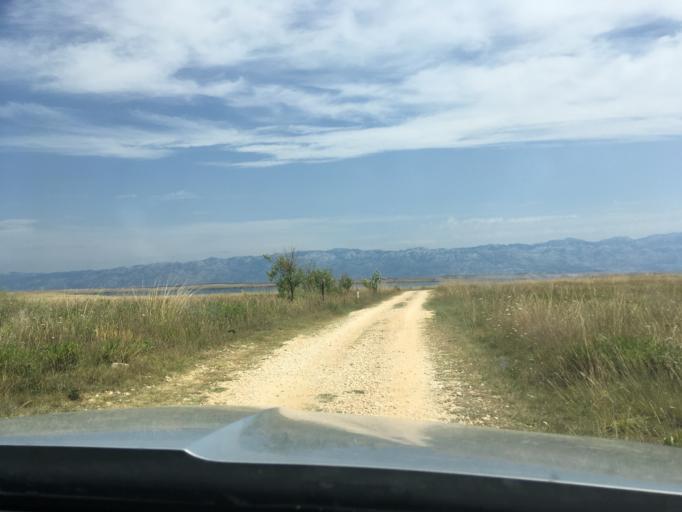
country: HR
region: Zadarska
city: Privlaka
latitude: 44.2671
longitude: 15.1514
